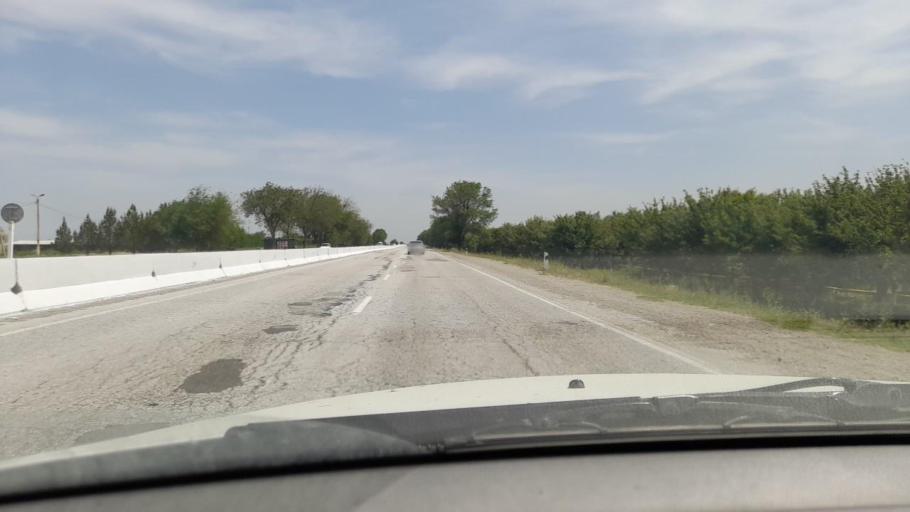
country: UZ
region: Navoiy
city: Konimex
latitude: 40.1145
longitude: 65.0967
